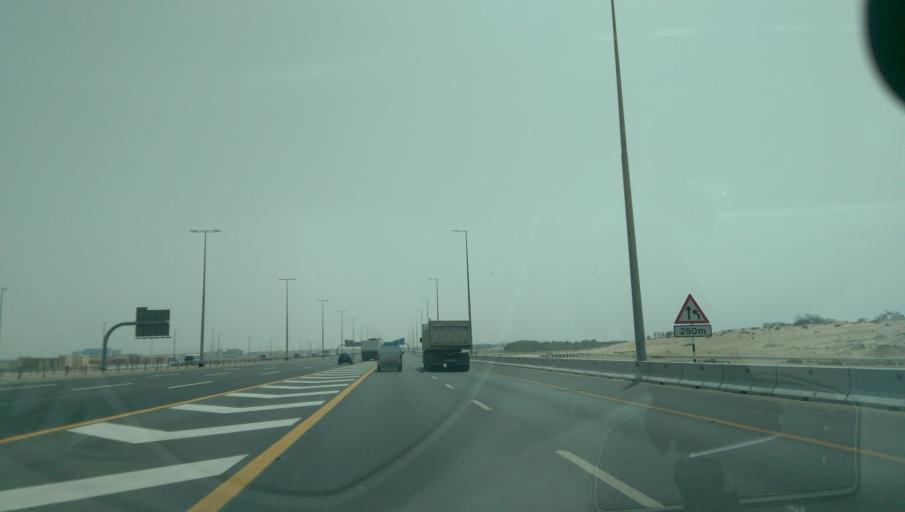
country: AE
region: Abu Dhabi
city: Abu Dhabi
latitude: 24.2984
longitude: 54.5843
